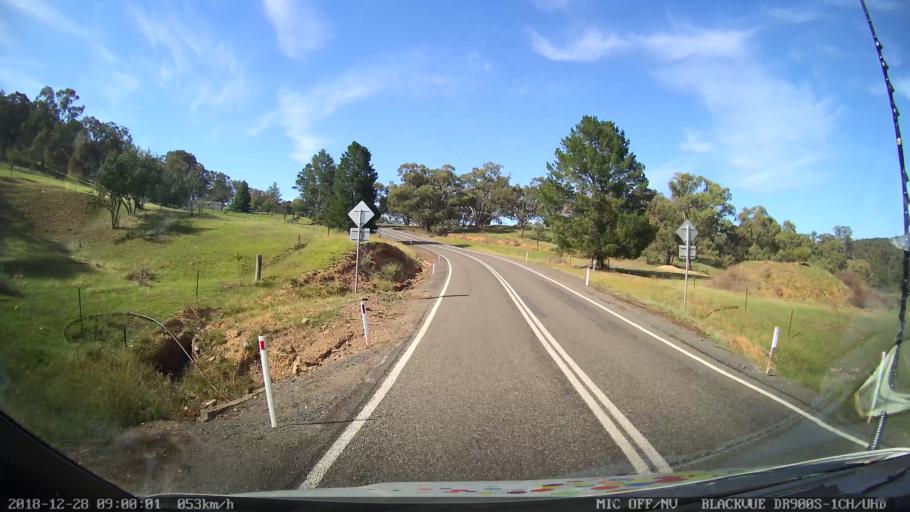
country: AU
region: New South Wales
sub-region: Upper Lachlan Shire
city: Crookwell
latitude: -34.1353
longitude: 149.3346
